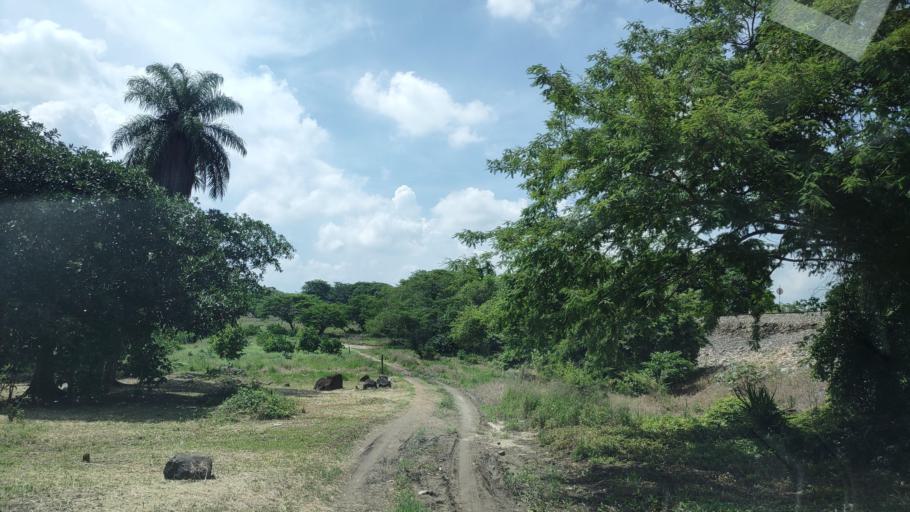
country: MX
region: Veracruz
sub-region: Coatepec
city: Bella Esperanza
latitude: 19.4294
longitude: -96.8109
